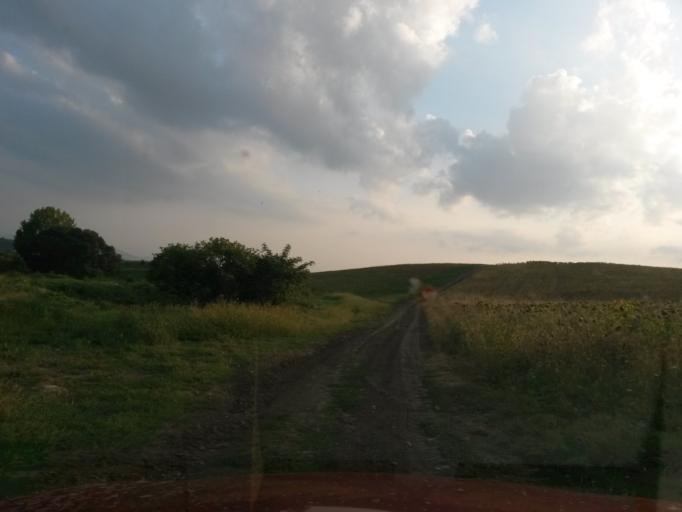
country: SK
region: Kosicky
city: Secovce
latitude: 48.8061
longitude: 21.4730
